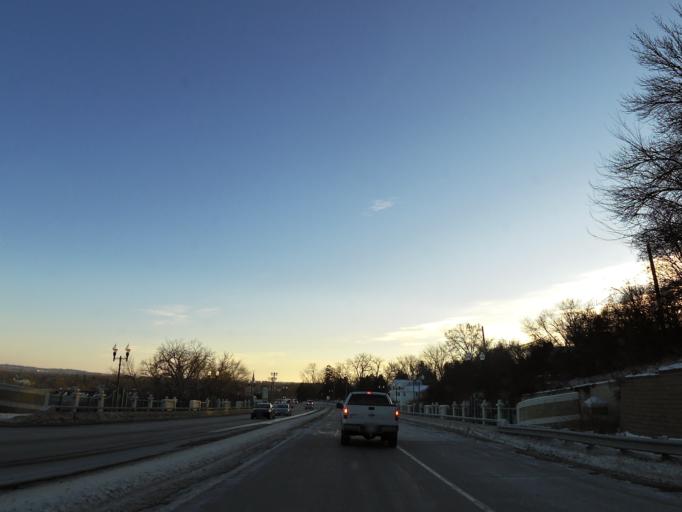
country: US
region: Minnesota
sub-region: Carver County
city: Chaska
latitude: 44.7950
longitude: -93.6017
